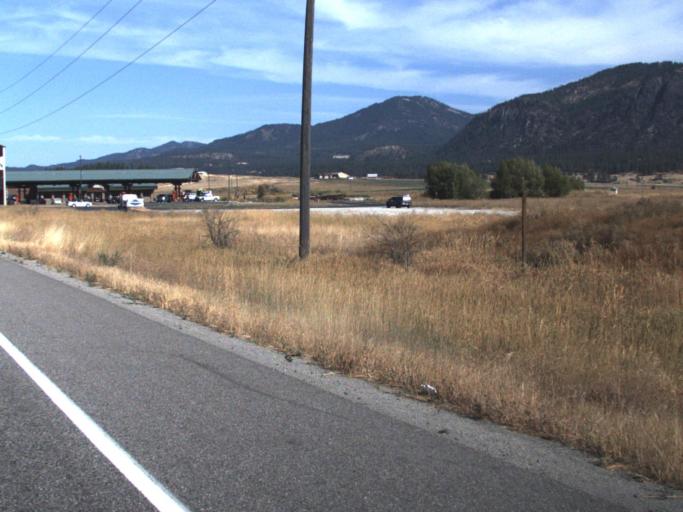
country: US
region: Washington
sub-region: Stevens County
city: Chewelah
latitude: 48.2390
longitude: -117.7152
